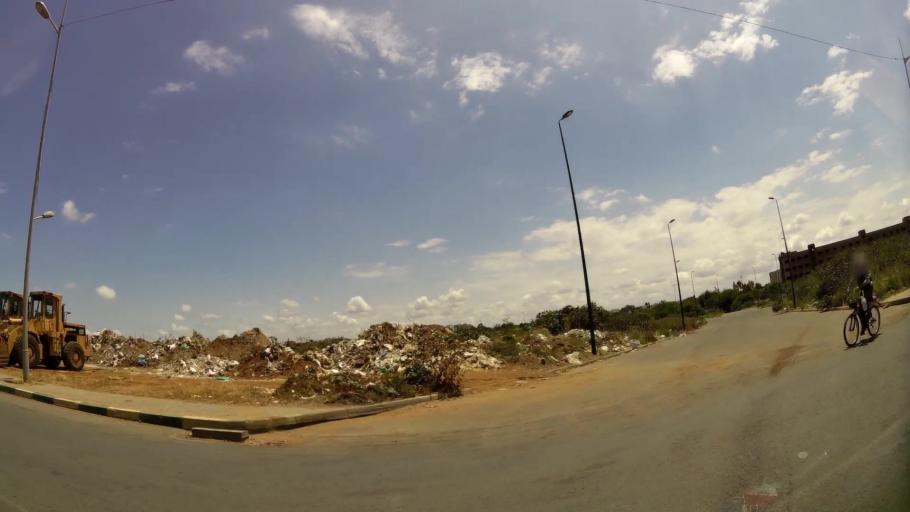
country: MA
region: Gharb-Chrarda-Beni Hssen
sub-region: Kenitra Province
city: Kenitra
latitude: 34.2589
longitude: -6.6118
